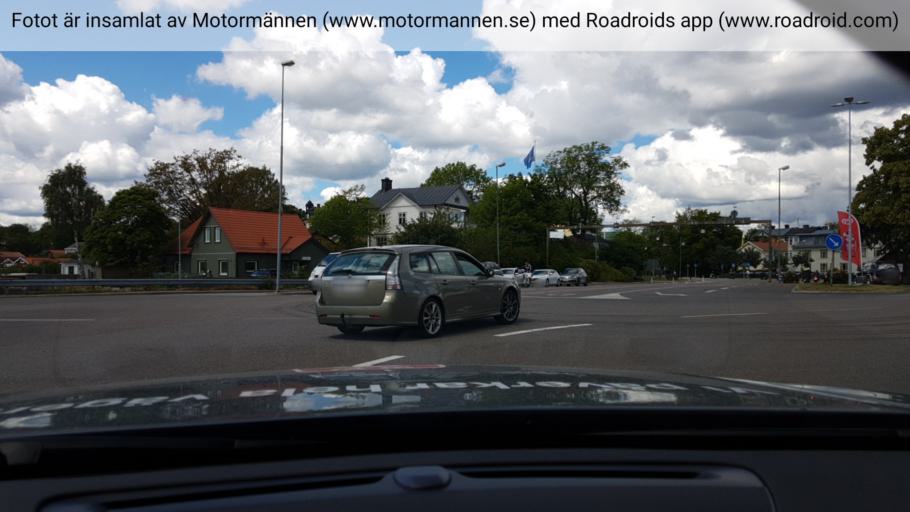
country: SE
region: Stockholm
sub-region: Vaxholms Kommun
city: Vaxholm
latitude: 59.4003
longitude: 18.3501
